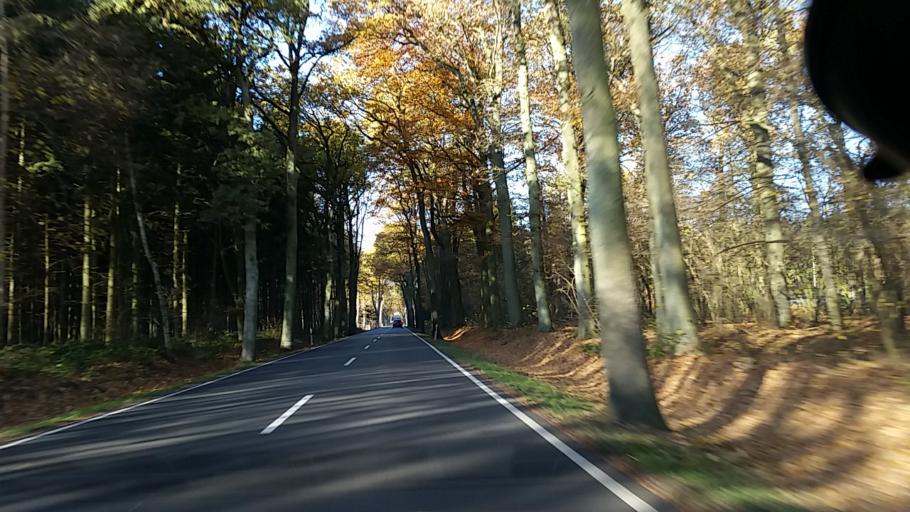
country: DE
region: Saxony-Anhalt
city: Jubar
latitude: 52.6786
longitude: 10.8368
